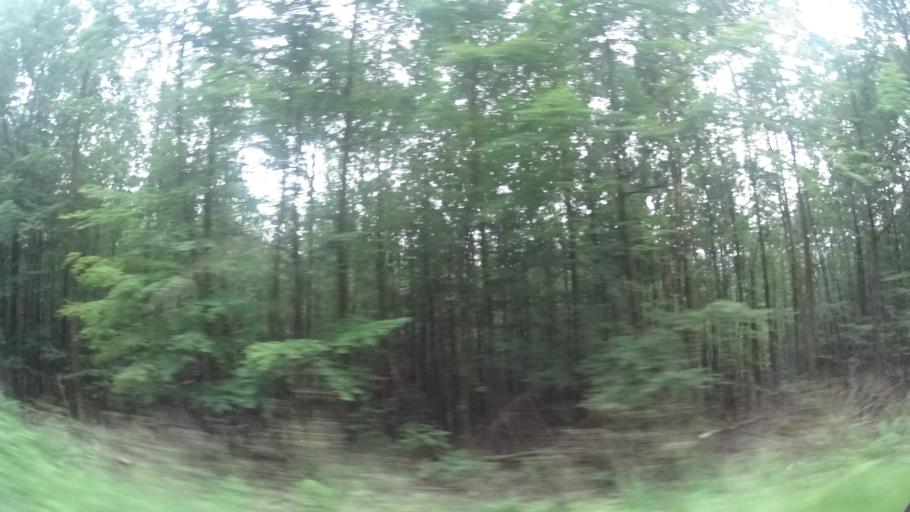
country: DE
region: Hesse
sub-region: Regierungsbezirk Darmstadt
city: Steinau an der Strasse
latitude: 50.2450
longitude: 9.4523
